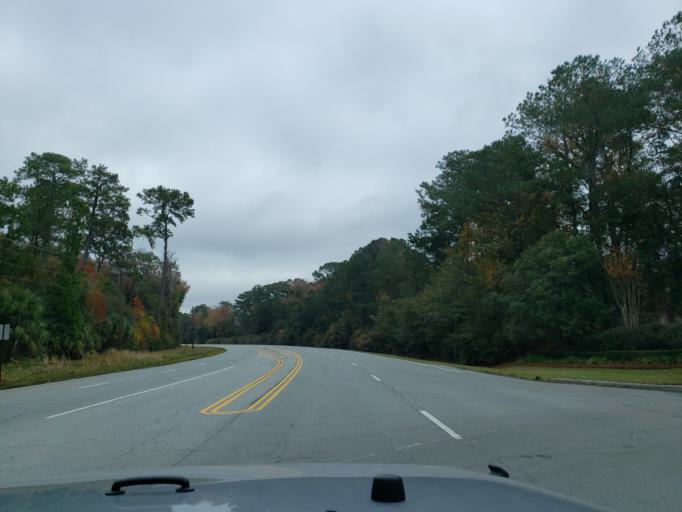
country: US
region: Georgia
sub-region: Chatham County
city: Whitemarsh Island
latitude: 32.0307
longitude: -80.9944
